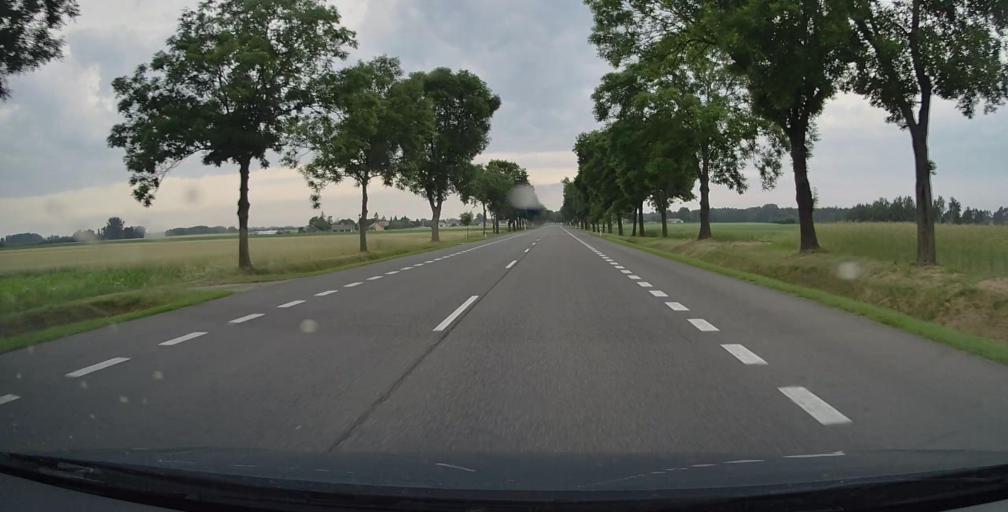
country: PL
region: Lublin Voivodeship
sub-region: Powiat lukowski
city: Trzebieszow
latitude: 52.0597
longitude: 22.5732
